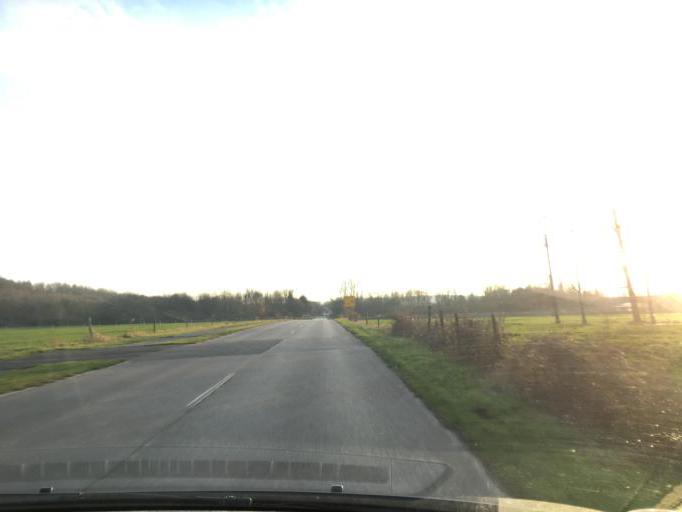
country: DE
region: North Rhine-Westphalia
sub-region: Regierungsbezirk Koln
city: Inden
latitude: 50.8558
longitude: 6.3612
